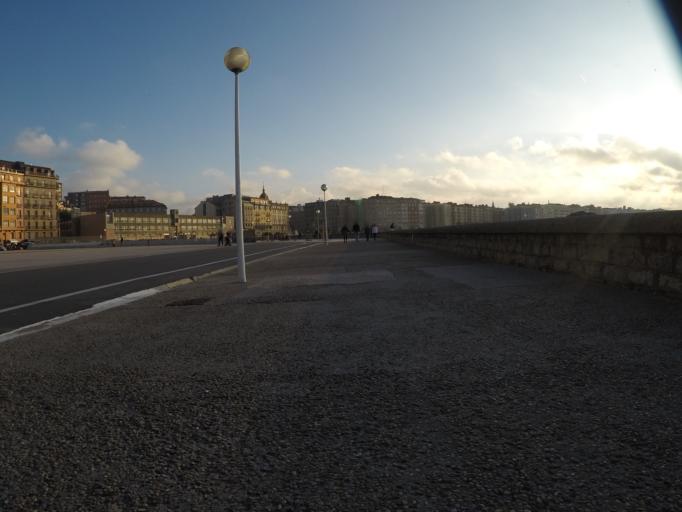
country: ES
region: Basque Country
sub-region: Provincia de Guipuzcoa
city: San Sebastian
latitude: 43.3290
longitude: -1.9717
